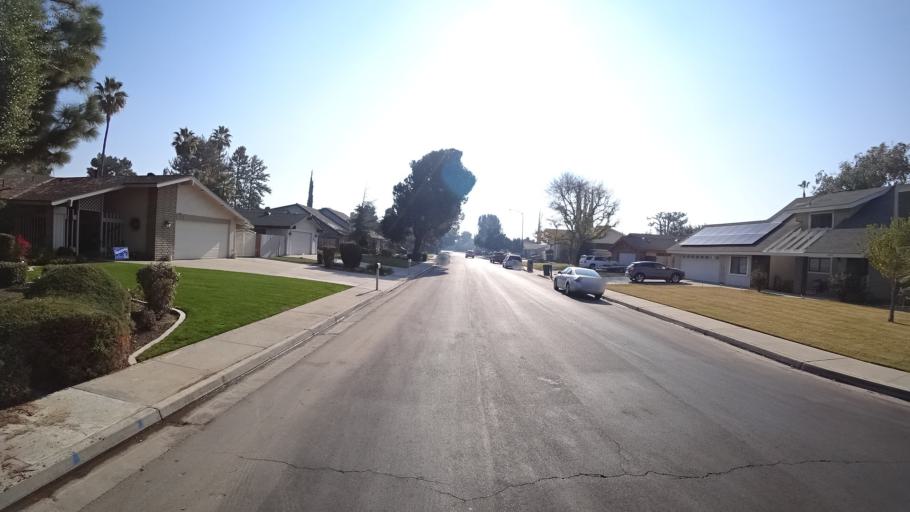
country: US
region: California
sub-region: Kern County
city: Greenacres
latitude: 35.3442
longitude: -119.0736
